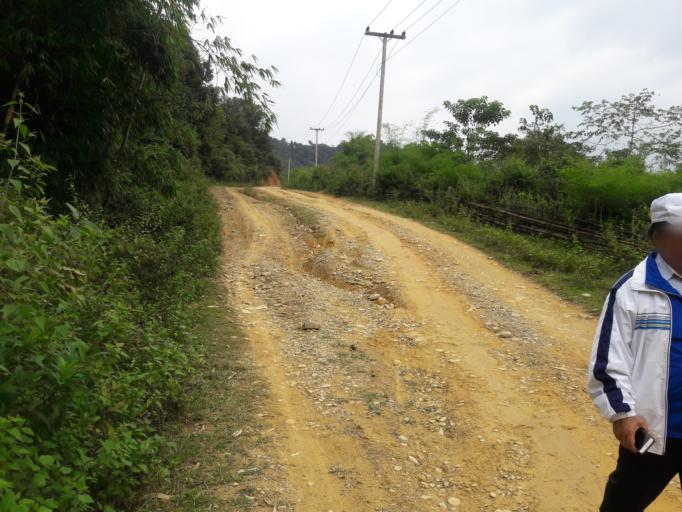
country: LA
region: Houaphan
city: Xam Nua
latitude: 20.3261
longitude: 104.0060
